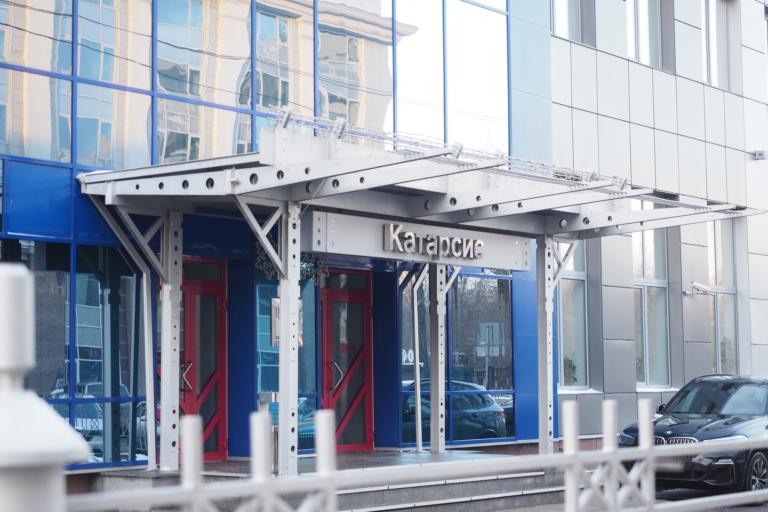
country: RU
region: St.-Petersburg
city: Novaya Derevnya
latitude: 59.9675
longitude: 30.2885
